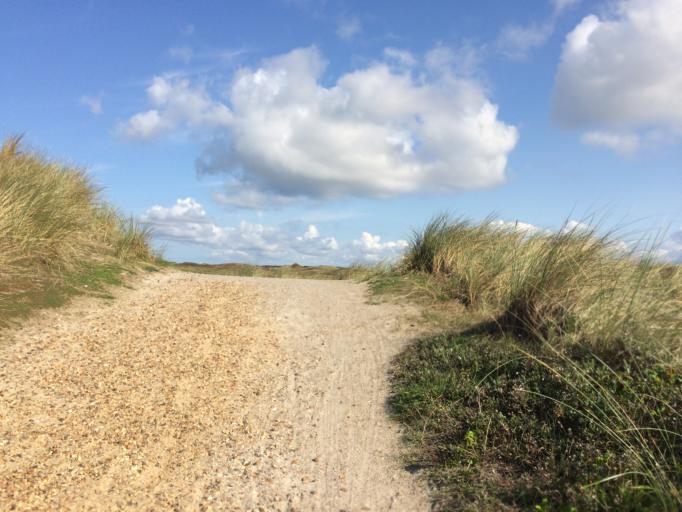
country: DK
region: Central Jutland
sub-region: Ringkobing-Skjern Kommune
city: Hvide Sande
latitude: 55.9305
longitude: 8.1510
